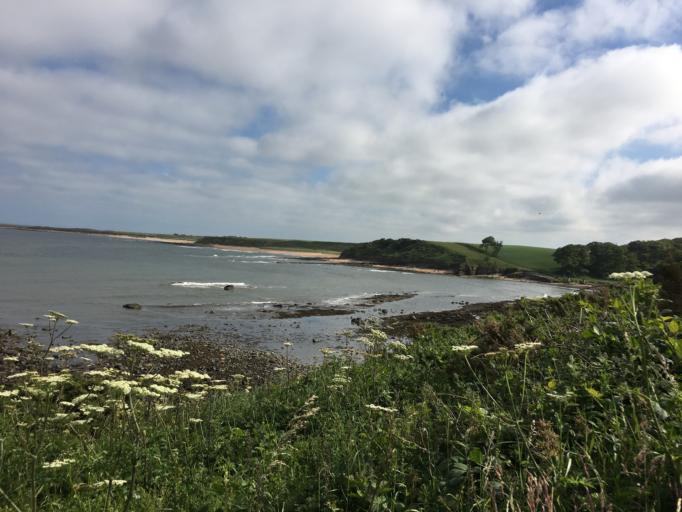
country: GB
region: England
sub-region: Northumberland
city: Alnmouth
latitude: 55.4427
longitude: -1.5915
